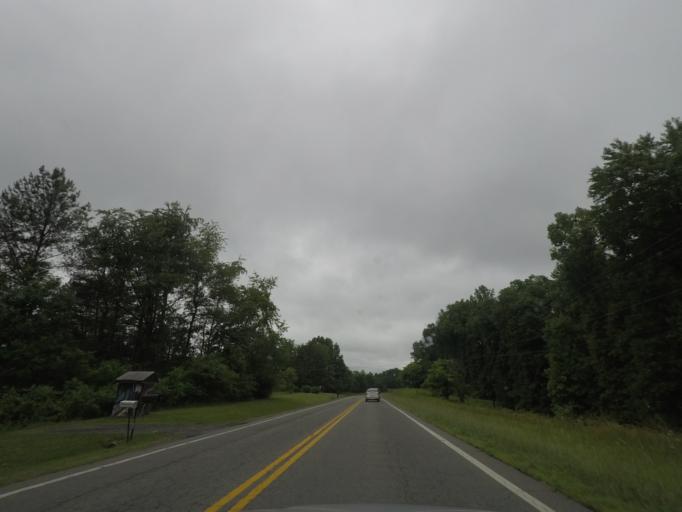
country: US
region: Virginia
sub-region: Fluvanna County
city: Weber City
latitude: 37.7919
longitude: -78.2393
